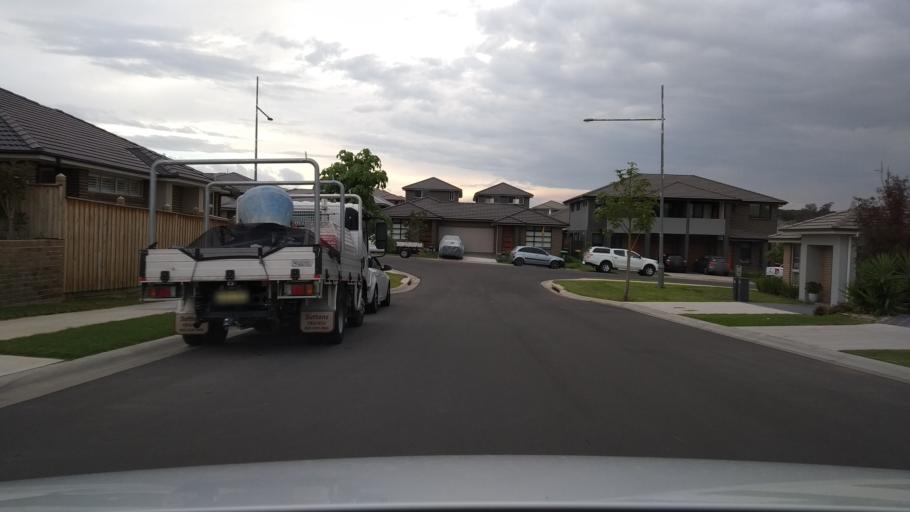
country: AU
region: New South Wales
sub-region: Camden
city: Narellan
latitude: -33.9992
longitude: 150.7291
